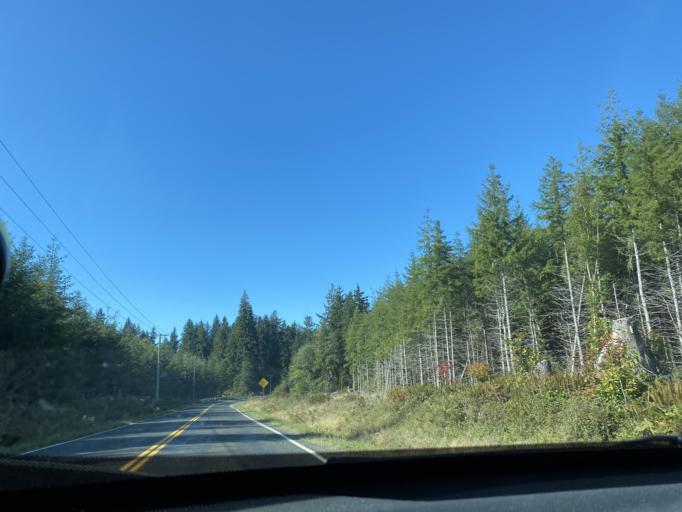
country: US
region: Washington
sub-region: Clallam County
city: Forks
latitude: 47.9521
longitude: -124.4642
